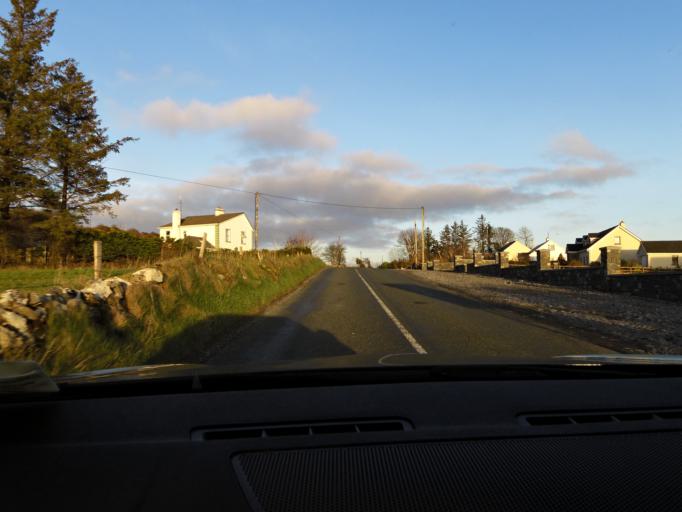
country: IE
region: Connaught
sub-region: Sligo
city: Tobercurry
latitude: 54.0469
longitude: -8.6842
